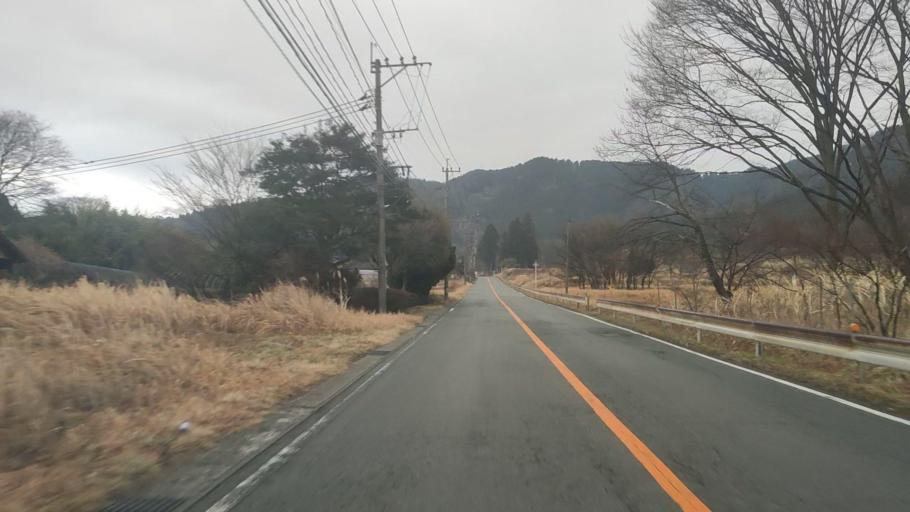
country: JP
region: Kumamoto
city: Aso
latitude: 32.8607
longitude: 131.1637
